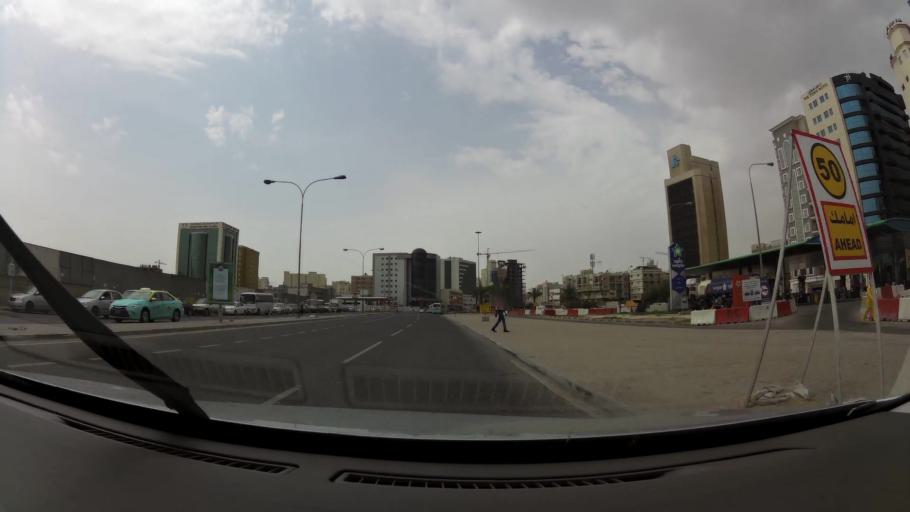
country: QA
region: Baladiyat ad Dawhah
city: Doha
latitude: 25.2797
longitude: 51.5303
